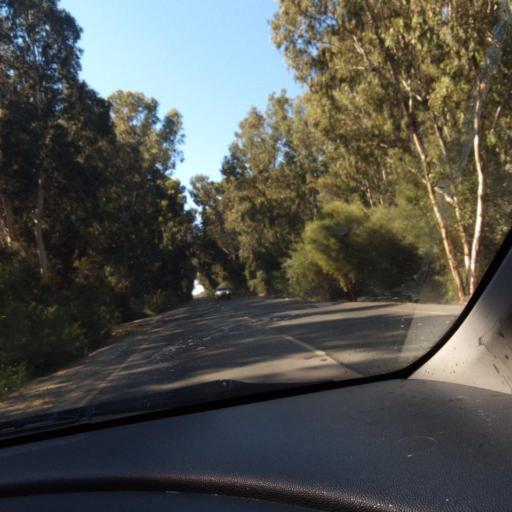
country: CY
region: Larnaka
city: Kolossi
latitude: 34.6274
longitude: 32.9477
